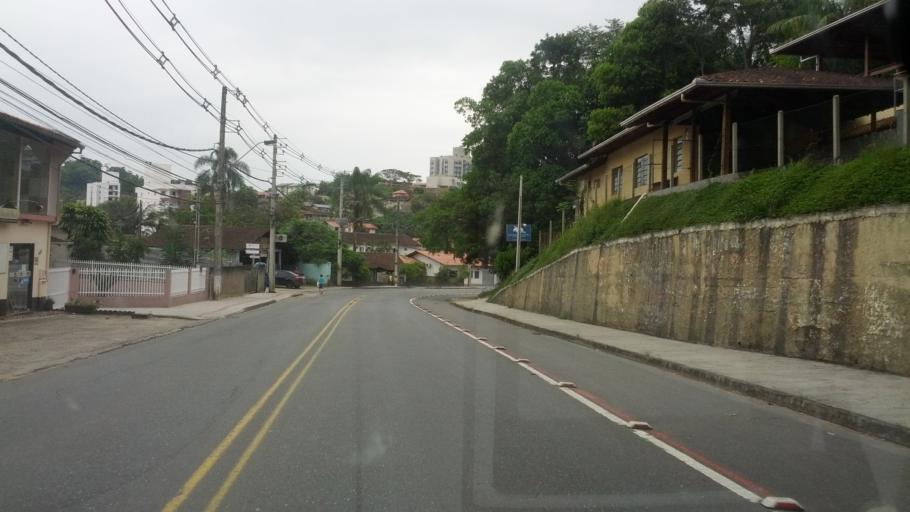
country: BR
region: Santa Catarina
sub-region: Blumenau
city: Blumenau
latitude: -26.9164
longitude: -49.1153
